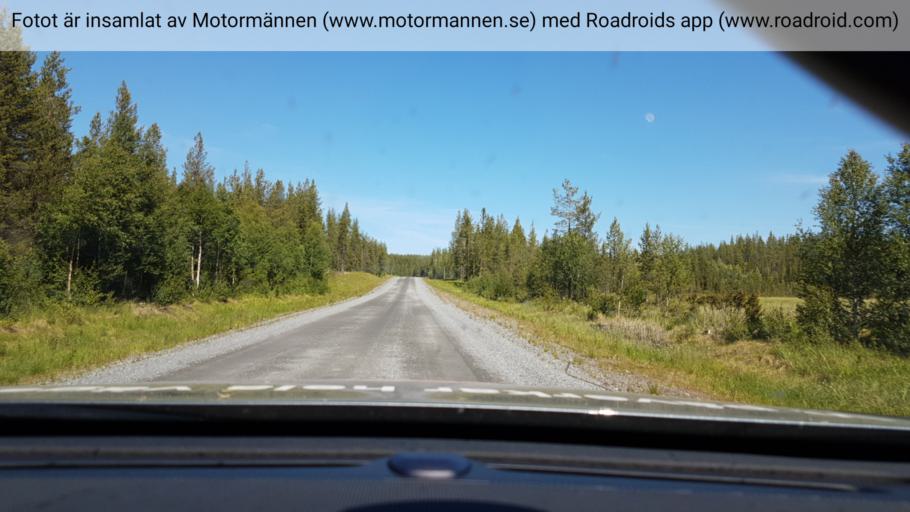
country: SE
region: Vaesterbotten
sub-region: Vilhelmina Kommun
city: Sjoberg
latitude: 64.6545
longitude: 15.7541
